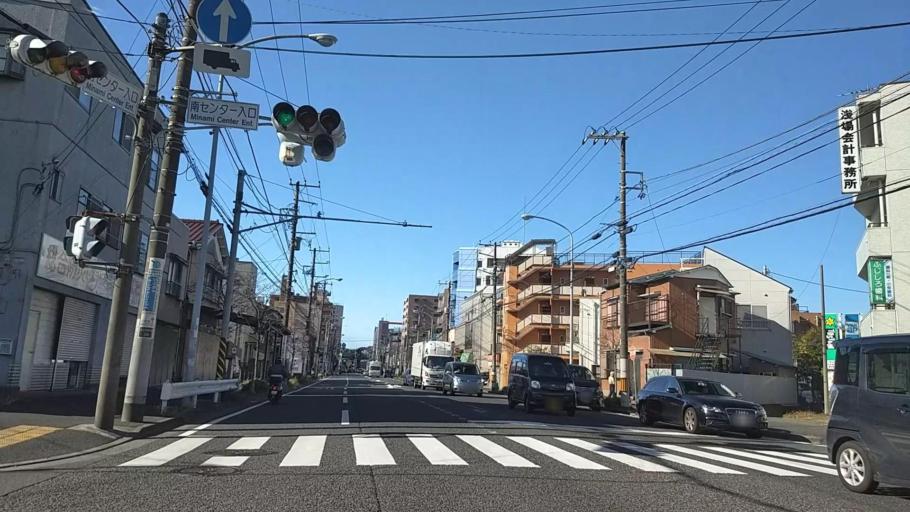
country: JP
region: Kanagawa
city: Yokohama
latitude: 35.4338
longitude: 139.6064
